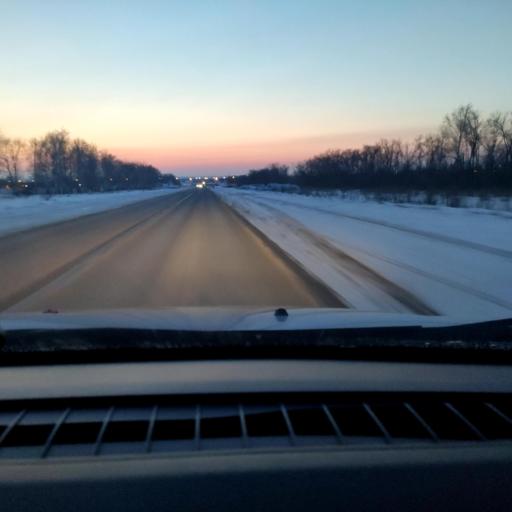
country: RU
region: Samara
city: Krasnyy Yar
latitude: 53.4727
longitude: 50.4155
